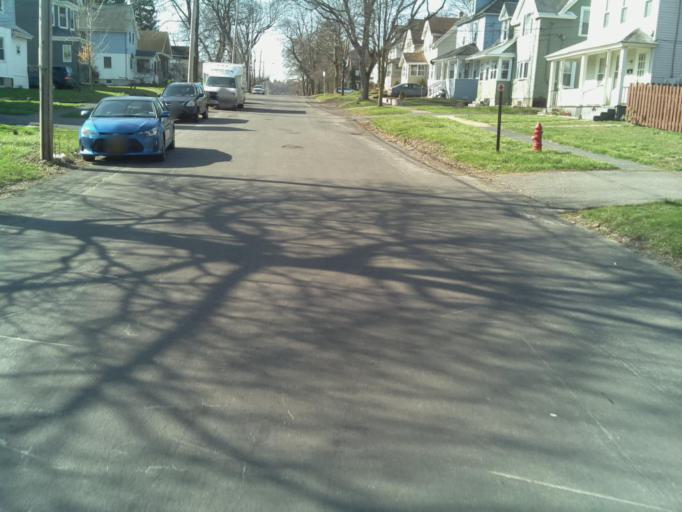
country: US
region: New York
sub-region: Onondaga County
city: Lyncourt
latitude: 43.0605
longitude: -76.1080
